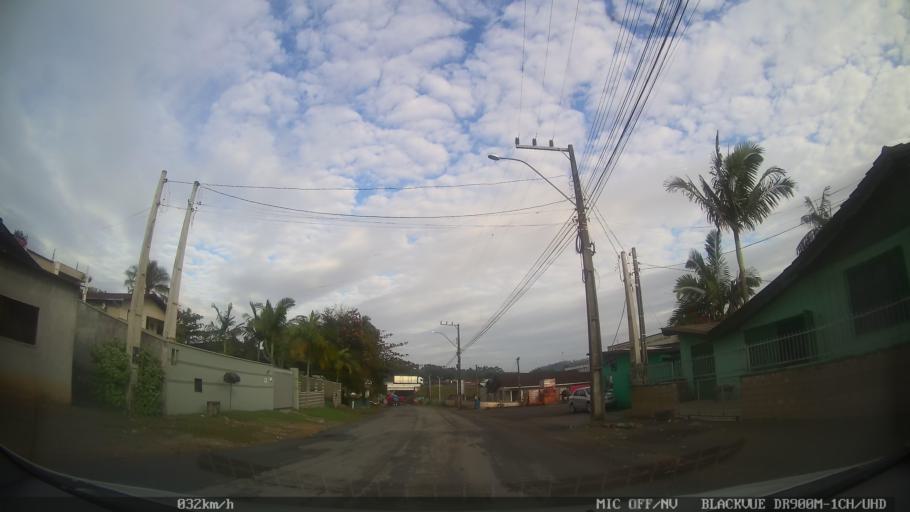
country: BR
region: Santa Catarina
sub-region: Barra Velha
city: Barra Velha
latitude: -26.6201
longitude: -48.7155
